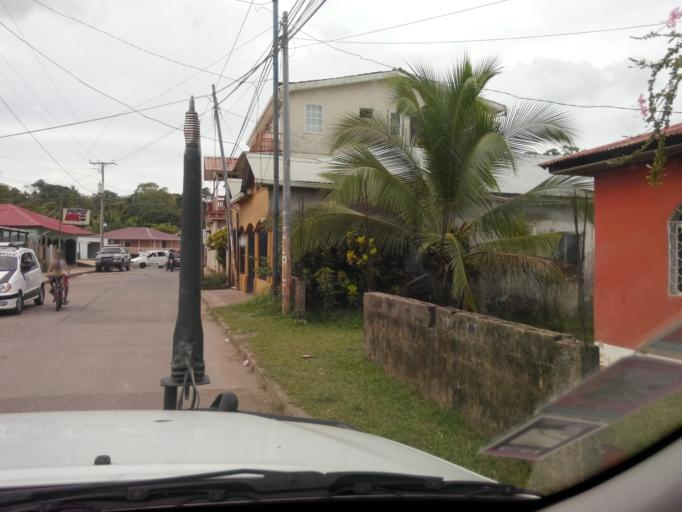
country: NI
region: Atlantico Sur
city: Bluefields
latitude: 12.0259
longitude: -83.7673
